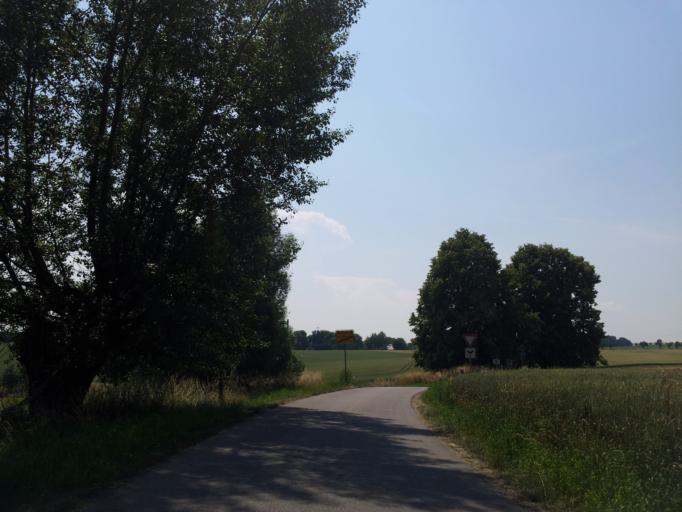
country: DE
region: Saxony
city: Burkau
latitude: 51.2048
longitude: 14.1962
